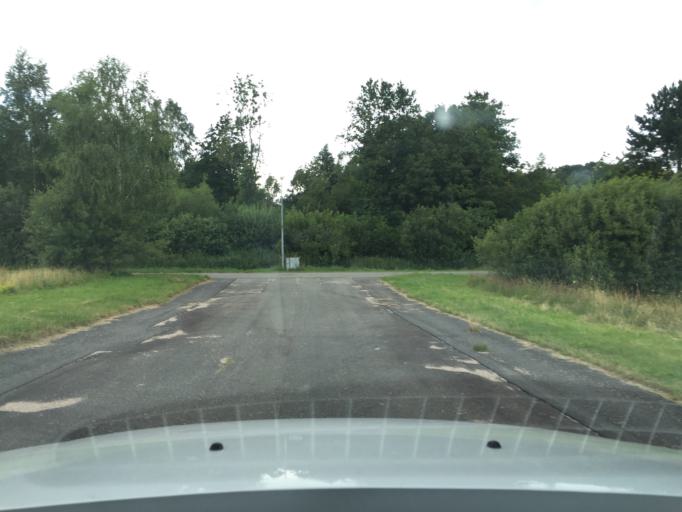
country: SE
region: Skane
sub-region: Hassleholms Kommun
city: Sosdala
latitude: 56.0455
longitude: 13.6723
